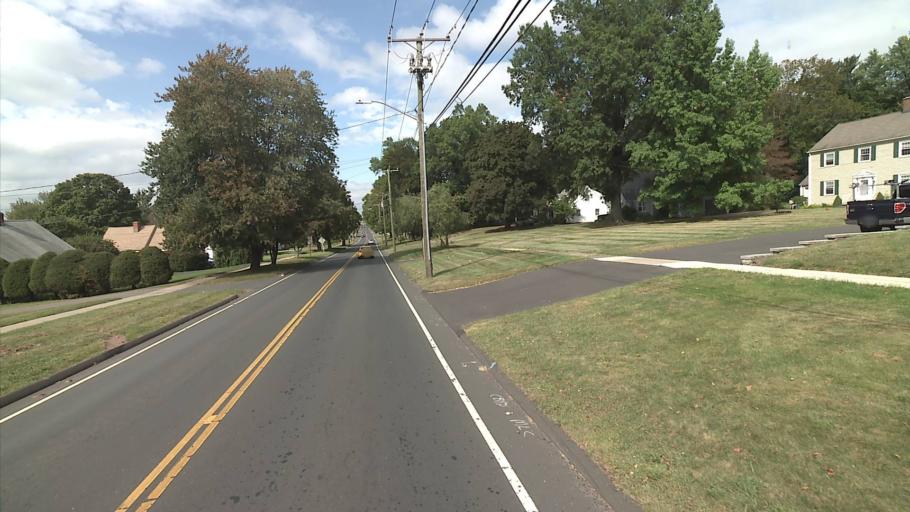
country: US
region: Connecticut
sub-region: Hartford County
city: Newington
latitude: 41.6874
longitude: -72.7213
